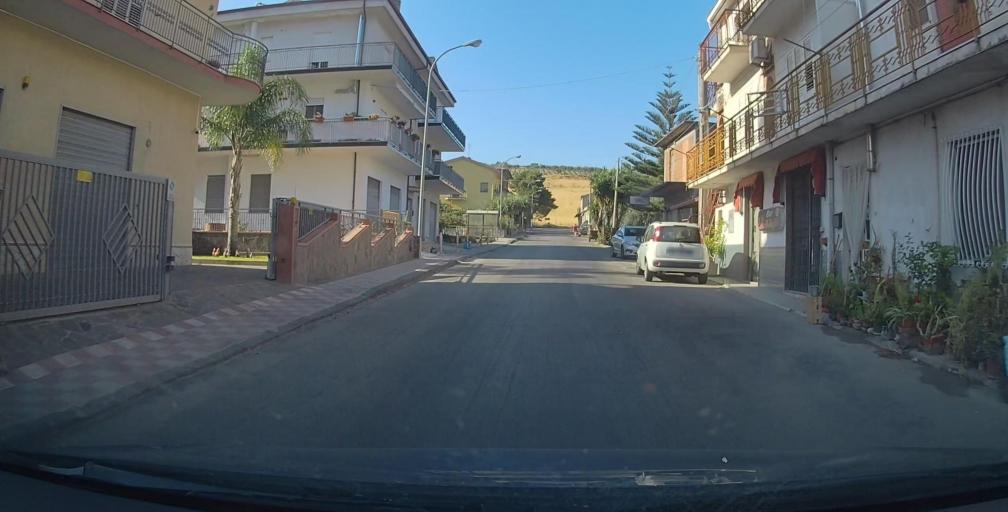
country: IT
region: Sicily
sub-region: Messina
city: San Piero Patti
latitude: 38.0770
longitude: 14.9802
